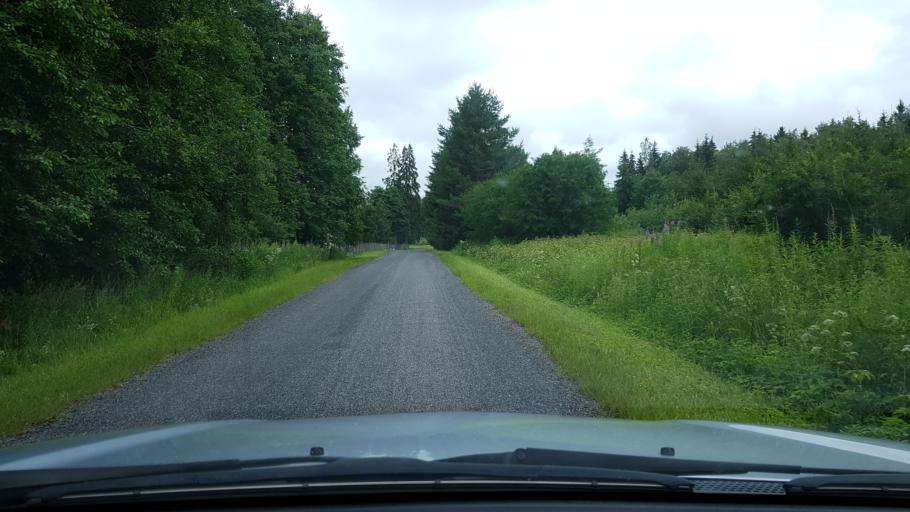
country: EE
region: Ida-Virumaa
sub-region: Narva-Joesuu linn
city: Narva-Joesuu
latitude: 59.3554
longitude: 28.0388
